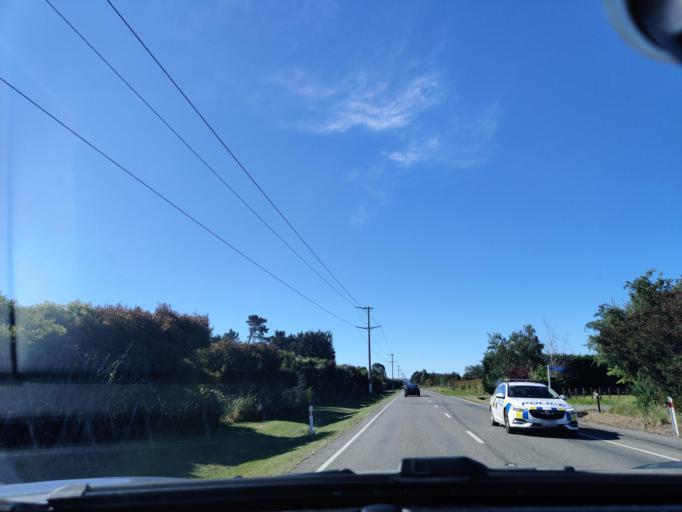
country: NZ
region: Wellington
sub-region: Masterton District
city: Masterton
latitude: -40.9210
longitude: 175.6419
